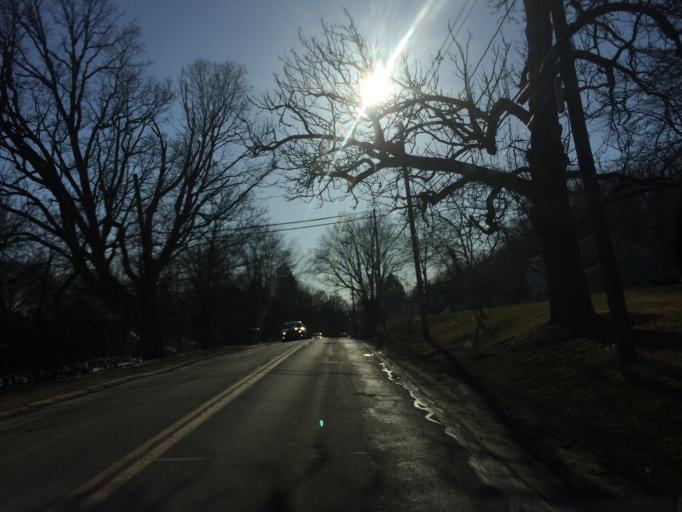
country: US
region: New York
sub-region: Monroe County
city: Brighton
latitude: 43.1334
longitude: -77.5840
